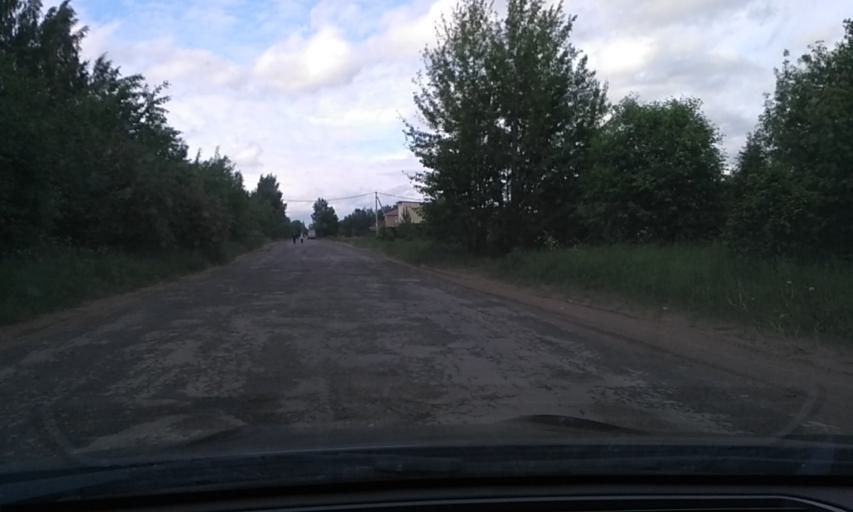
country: RU
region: Leningrad
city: Otradnoye
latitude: 59.7898
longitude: 30.7916
